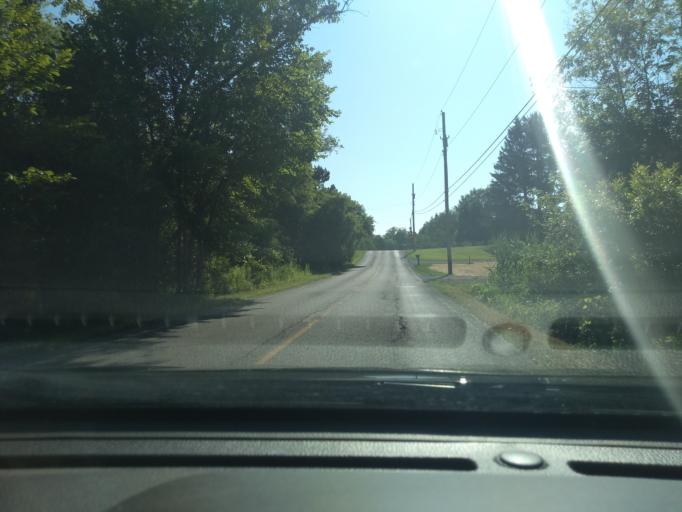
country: US
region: New York
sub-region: Erie County
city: Orchard Park
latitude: 42.7896
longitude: -78.6933
